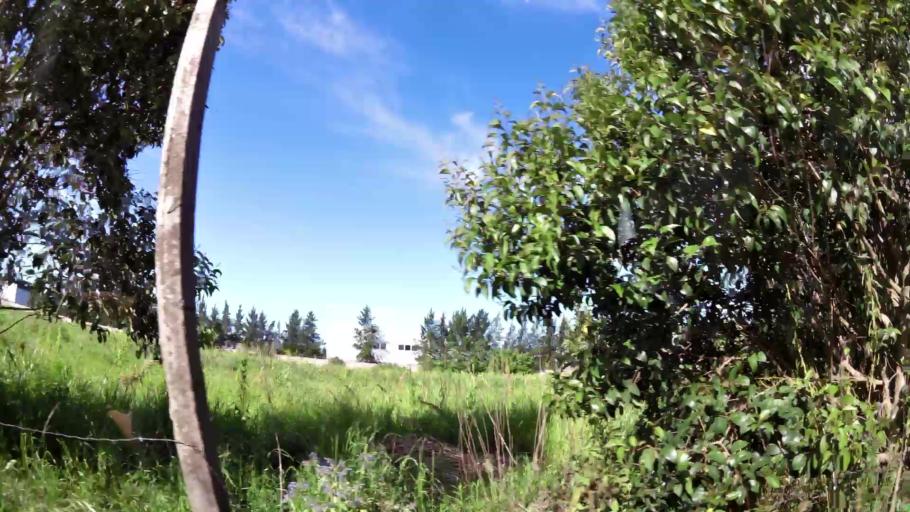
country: AR
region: Buenos Aires
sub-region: Partido de Quilmes
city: Quilmes
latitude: -34.7846
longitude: -58.2378
